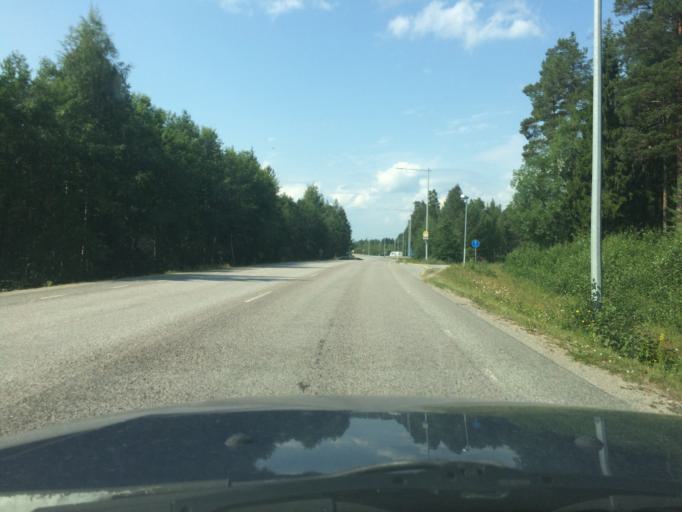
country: SE
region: Norrbotten
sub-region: Pitea Kommun
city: Pitea
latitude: 65.3312
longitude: 21.4509
